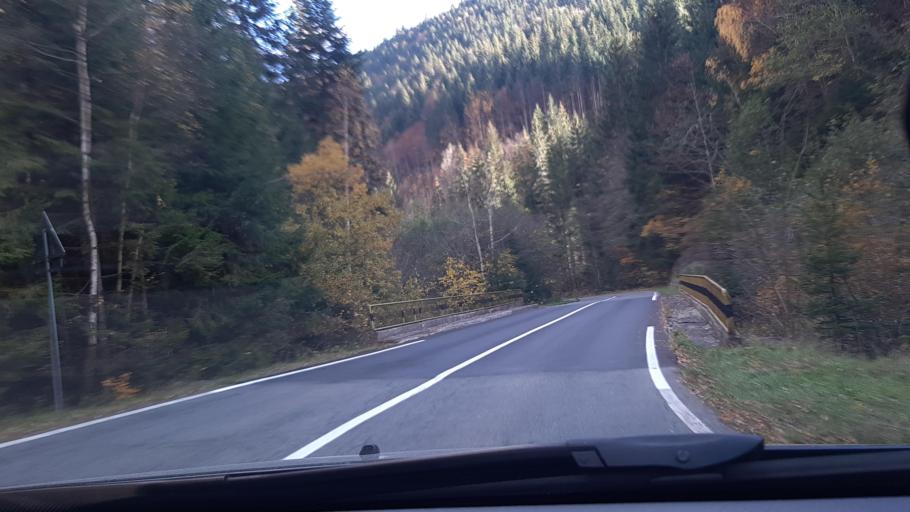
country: RO
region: Valcea
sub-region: Comuna Voineasa
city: Voineasa
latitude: 45.4368
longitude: 23.8642
